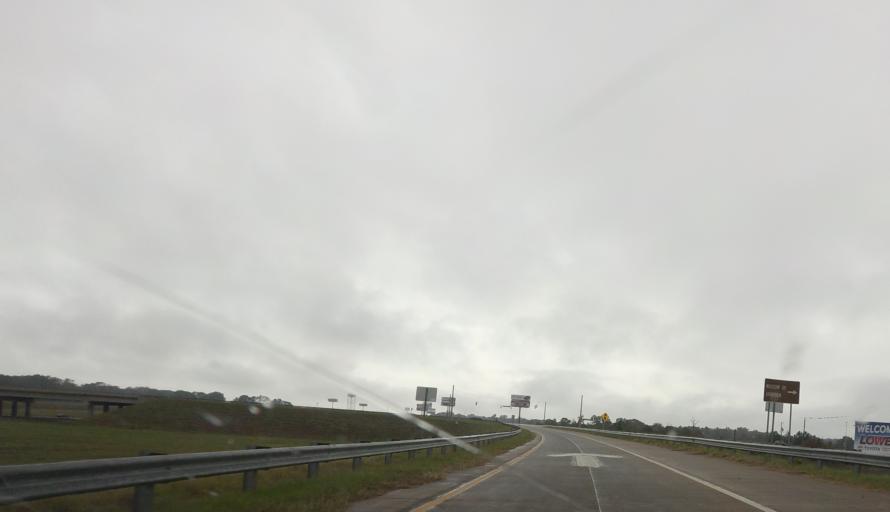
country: US
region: Georgia
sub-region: Houston County
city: Centerville
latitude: 32.5856
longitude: -83.7413
